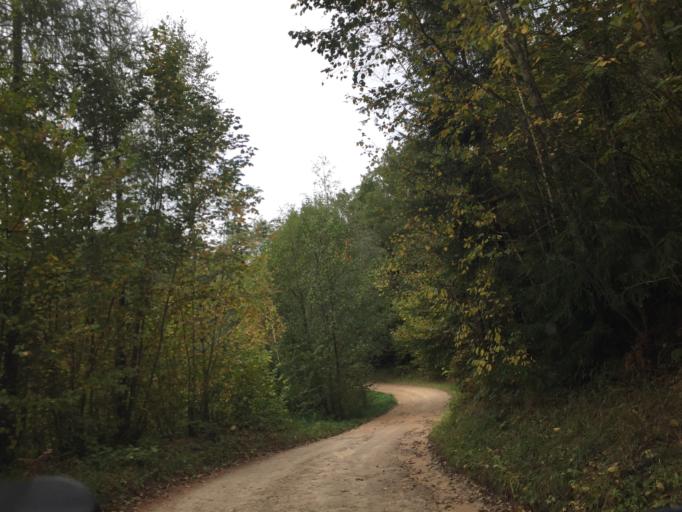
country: LV
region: Auces Novads
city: Auce
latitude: 56.5528
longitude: 23.0290
